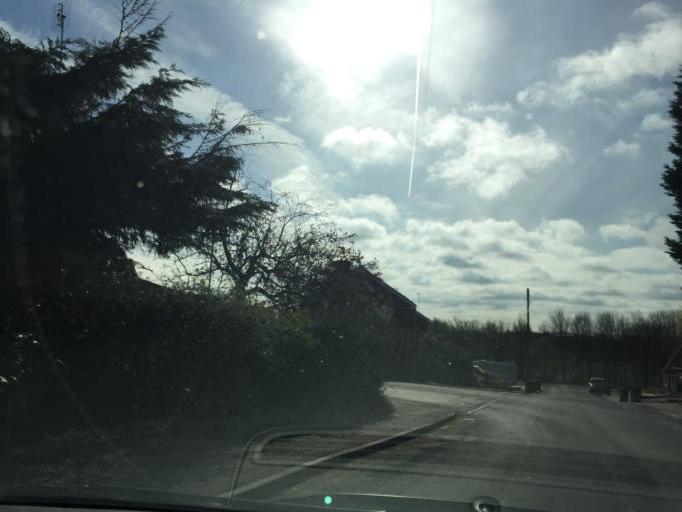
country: GB
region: England
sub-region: Coventry
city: Coventry
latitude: 52.3846
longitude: -1.4986
